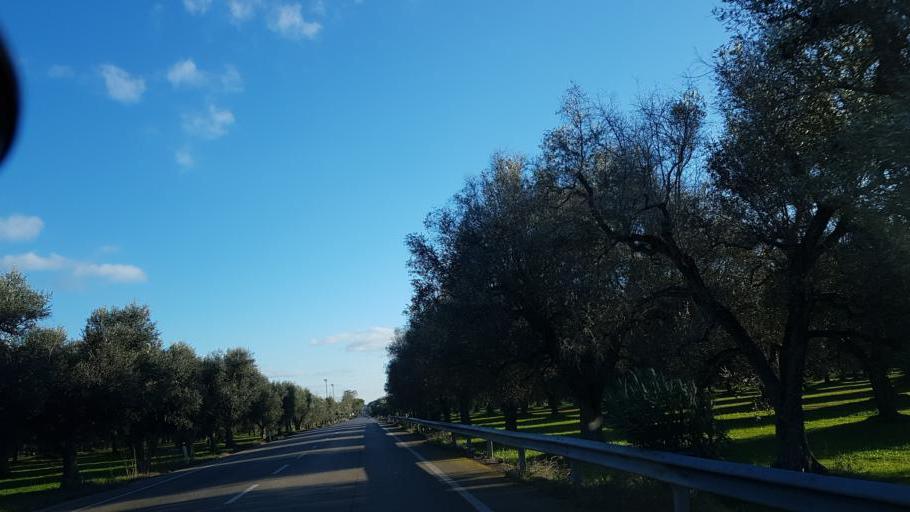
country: IT
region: Apulia
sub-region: Provincia di Lecce
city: Squinzano
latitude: 40.4491
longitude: 18.0296
